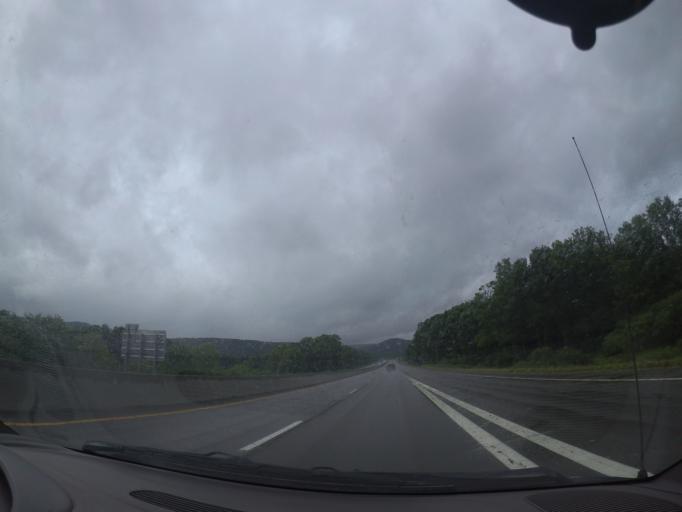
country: US
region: New York
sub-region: Cattaraugus County
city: Salamanca
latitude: 42.0894
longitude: -78.6360
